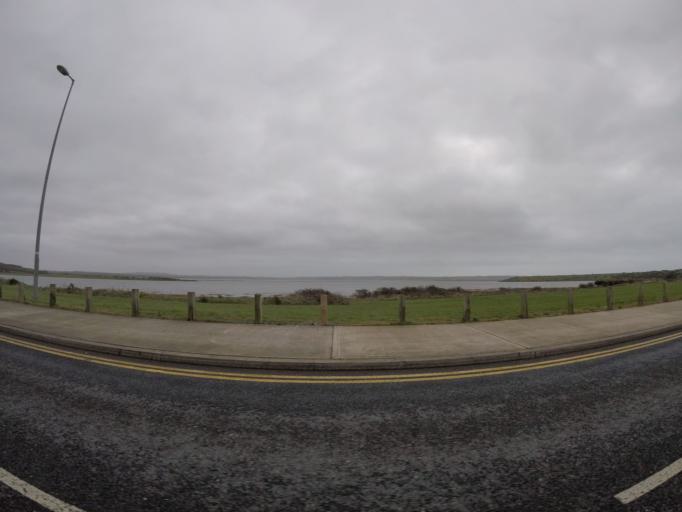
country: IE
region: Munster
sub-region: Waterford
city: Tra Mhor
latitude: 52.1658
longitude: -7.1329
